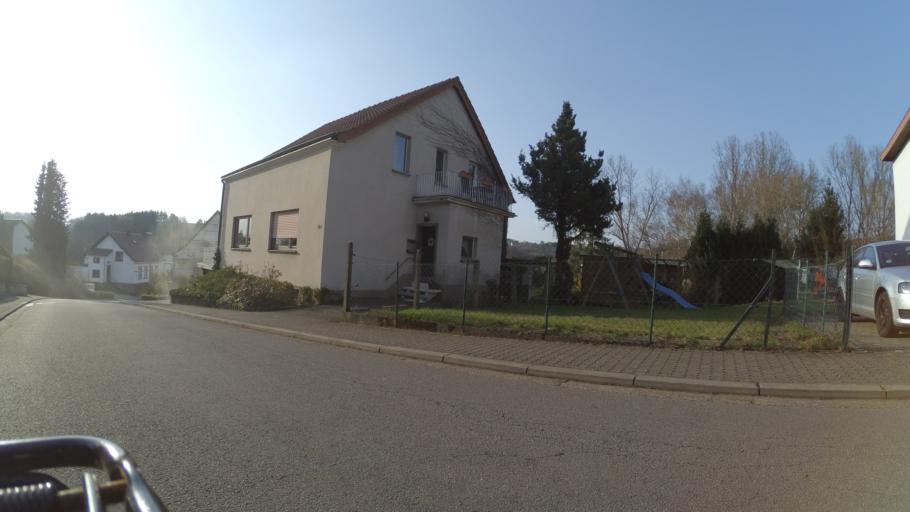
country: DE
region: Saarland
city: Heusweiler
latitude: 49.3459
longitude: 6.9880
